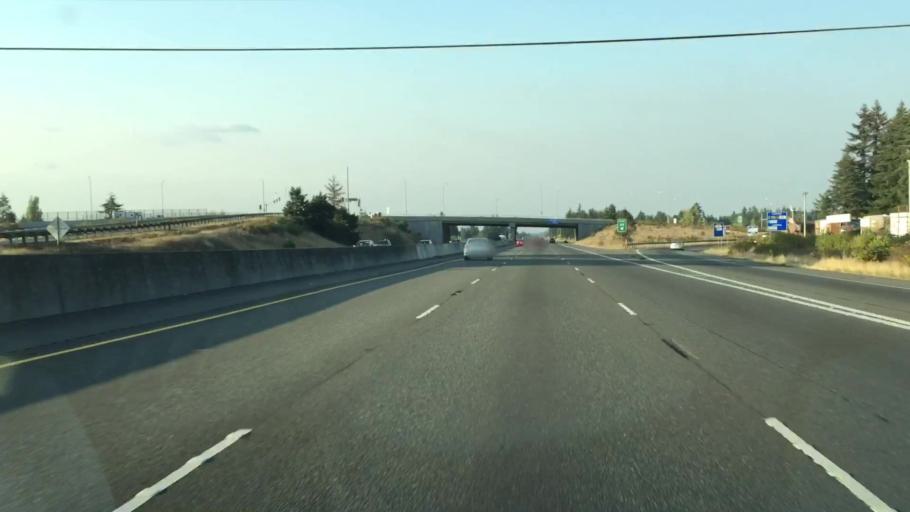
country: US
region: Washington
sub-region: Thurston County
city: Grand Mound
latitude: 46.8001
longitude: -123.0084
